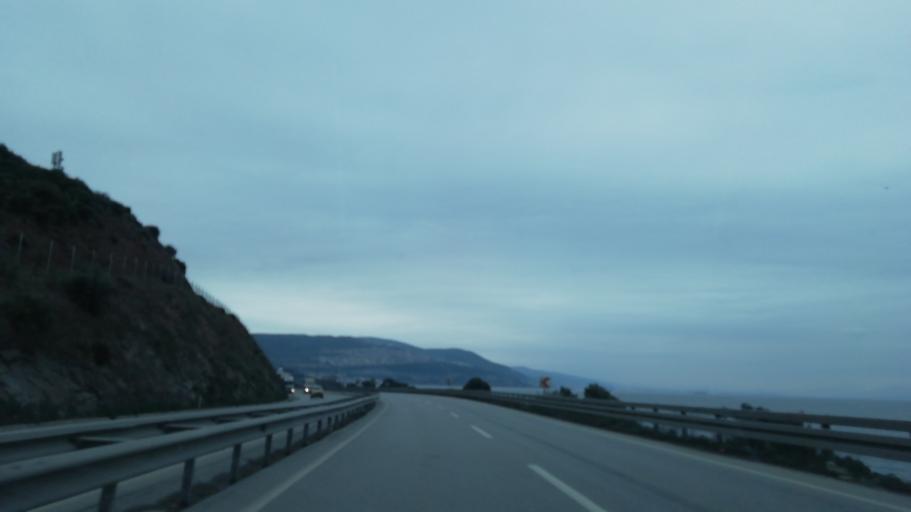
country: TR
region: Kocaeli
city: Tavsancil
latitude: 40.7689
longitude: 29.5782
